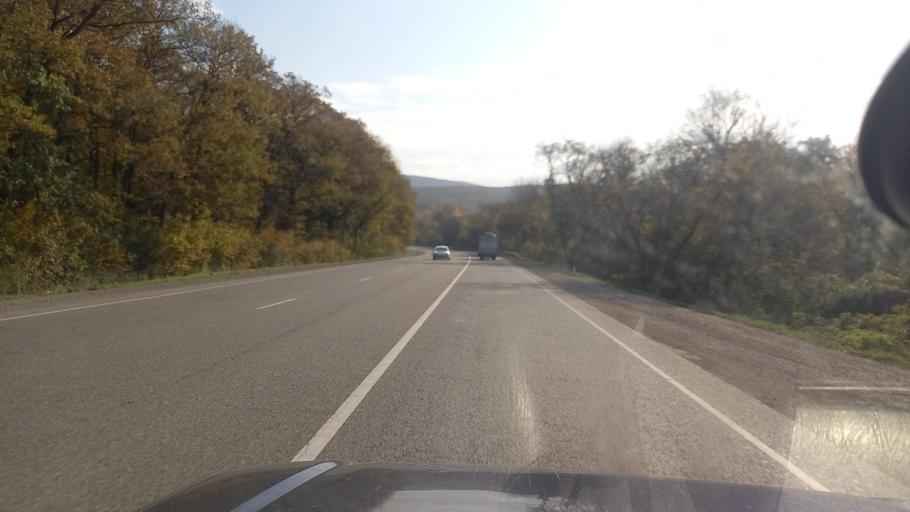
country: RU
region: Krasnodarskiy
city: Verkhnebakanskiy
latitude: 44.8420
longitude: 37.7034
